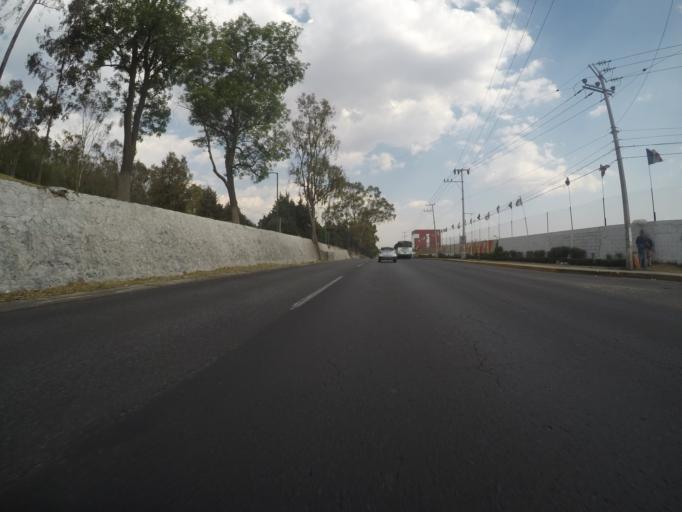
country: MX
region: Morelos
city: Metepec
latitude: 19.2459
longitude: -99.6069
